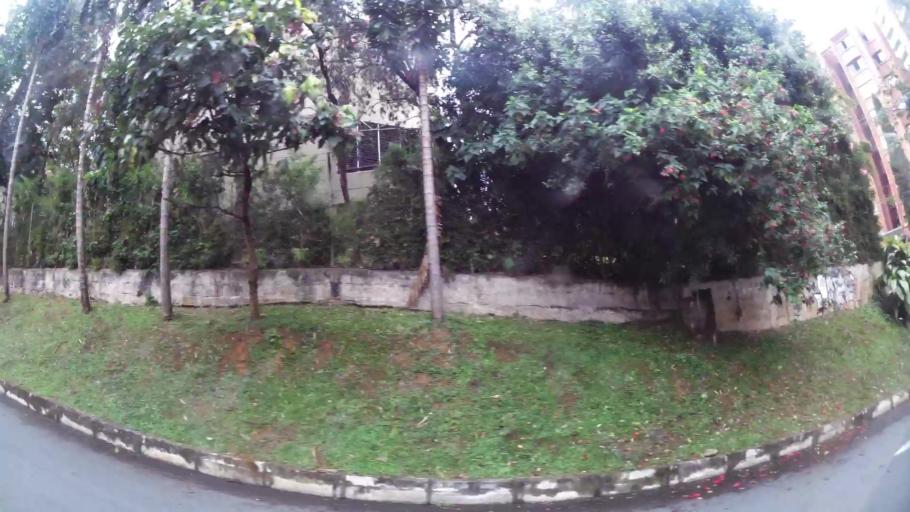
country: CO
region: Antioquia
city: Medellin
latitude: 6.2087
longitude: -75.5575
